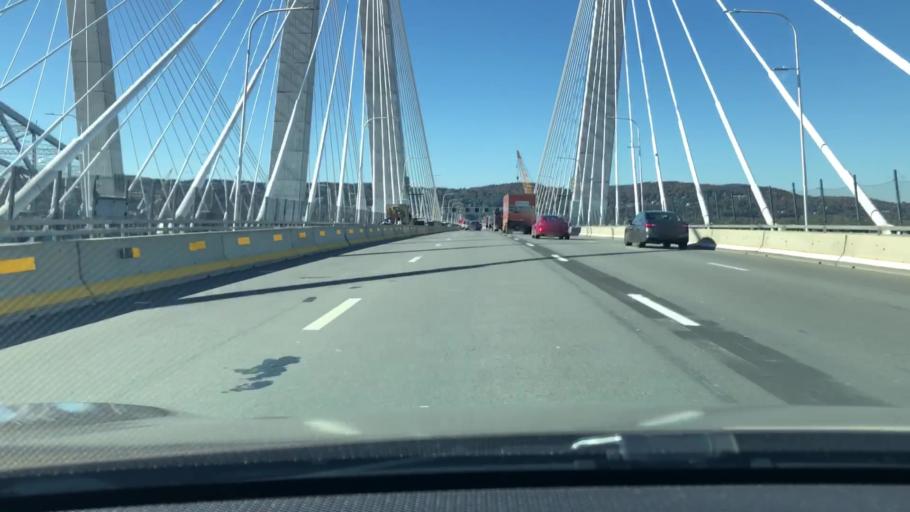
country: US
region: New York
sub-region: Westchester County
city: Tarrytown
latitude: 41.0713
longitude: -73.8814
